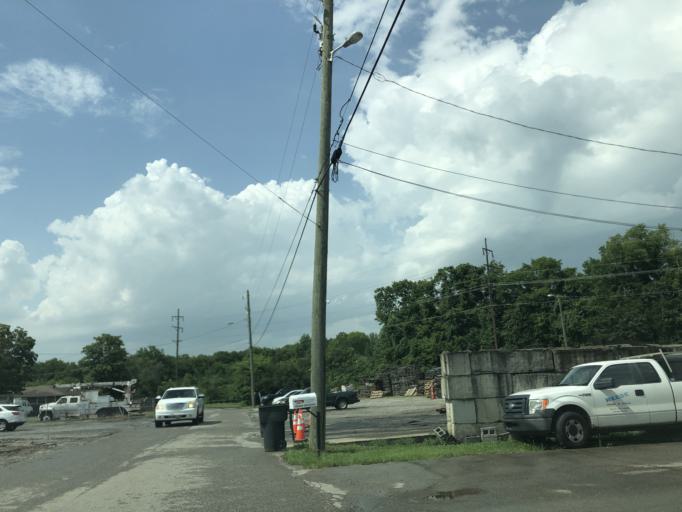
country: US
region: Tennessee
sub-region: Davidson County
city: Lakewood
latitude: 36.1725
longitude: -86.6736
